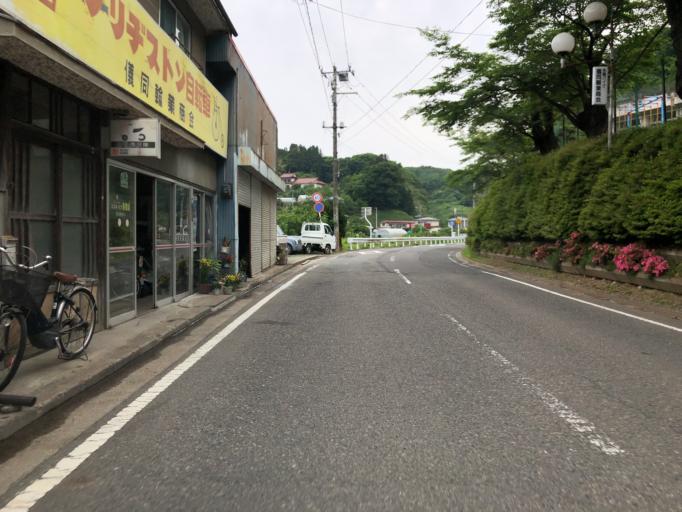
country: JP
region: Fukushima
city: Miharu
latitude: 37.4566
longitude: 140.5228
